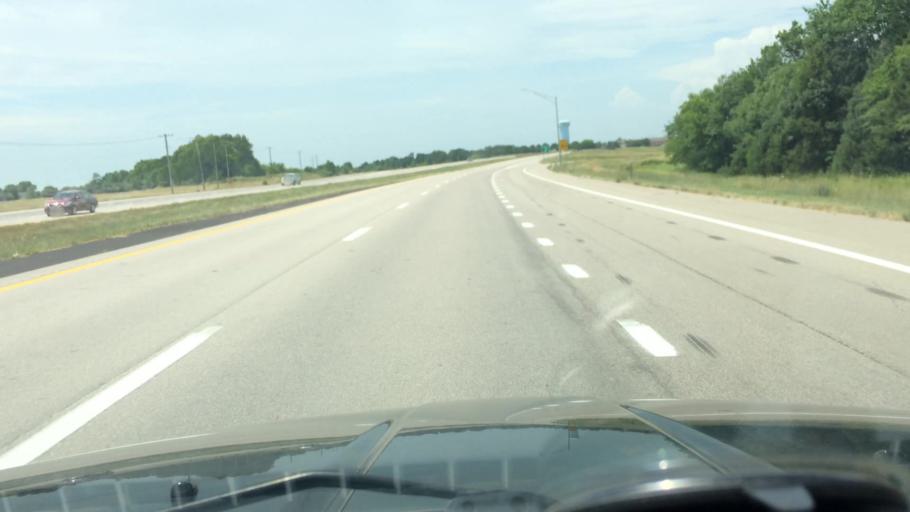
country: US
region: Missouri
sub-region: Polk County
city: Bolivar
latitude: 37.5899
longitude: -93.4274
